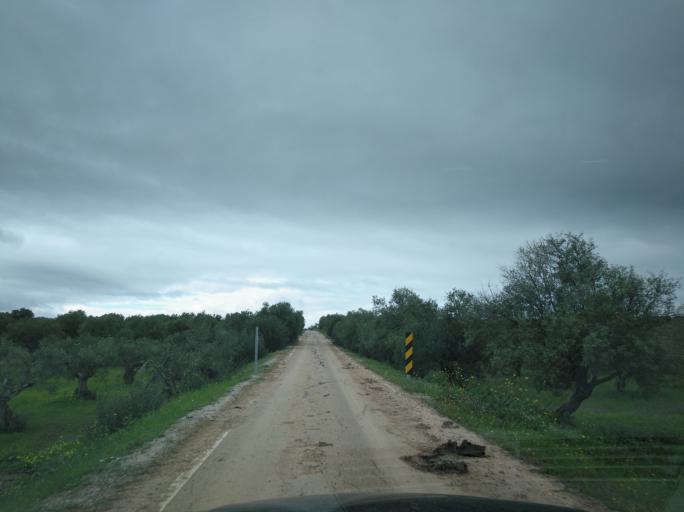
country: PT
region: Portalegre
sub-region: Campo Maior
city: Campo Maior
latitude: 38.9850
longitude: -7.0383
